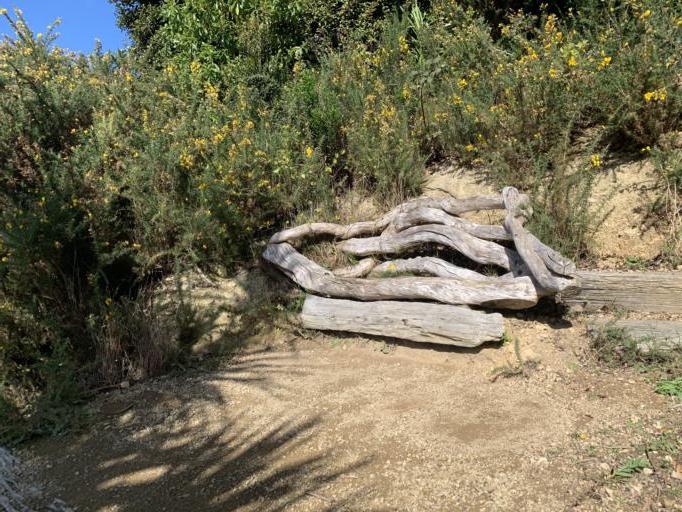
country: NZ
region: Wellington
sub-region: Wellington City
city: Brooklyn
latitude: -41.2992
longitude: 174.7537
